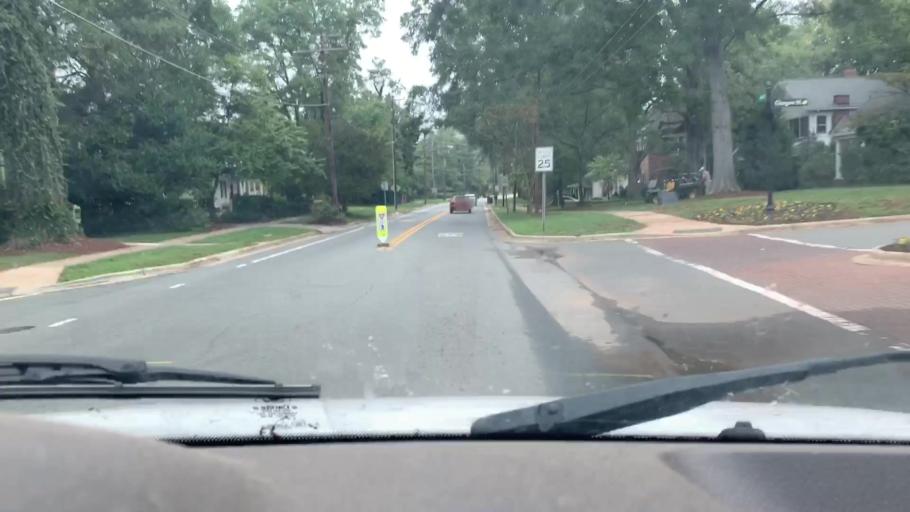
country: US
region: North Carolina
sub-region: Gaston County
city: Davidson
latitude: 35.5032
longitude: -80.8467
